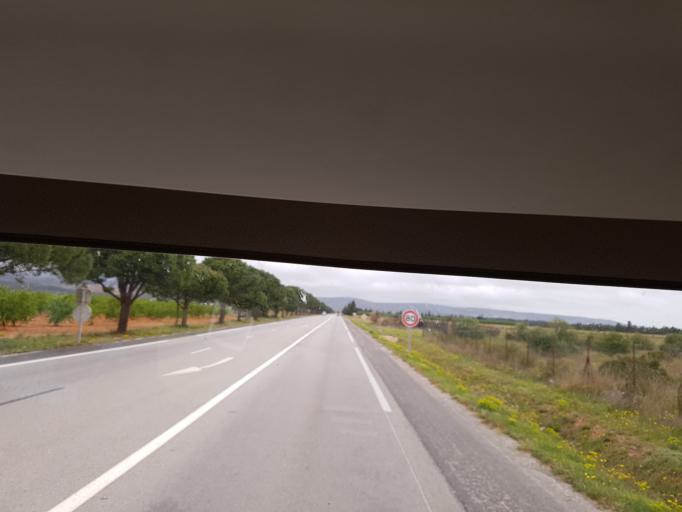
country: FR
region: Languedoc-Roussillon
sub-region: Departement des Pyrenees-Orientales
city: Salses-le-Chateau
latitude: 42.8115
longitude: 2.9134
